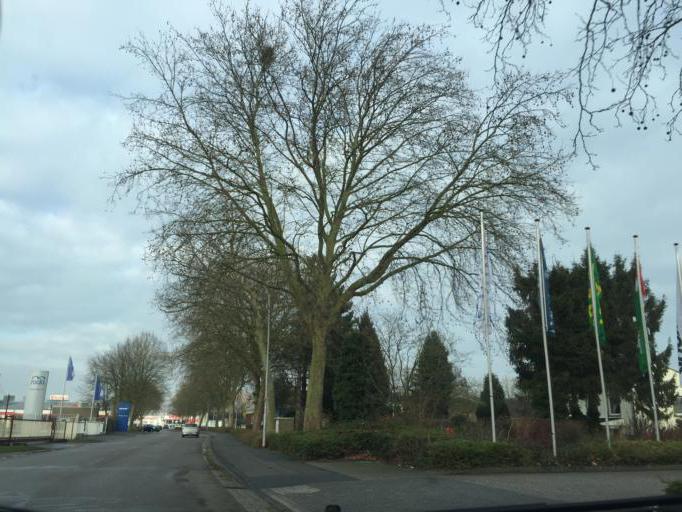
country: DE
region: North Rhine-Westphalia
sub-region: Regierungsbezirk Dusseldorf
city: Kleve
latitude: 51.7969
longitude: 6.1397
